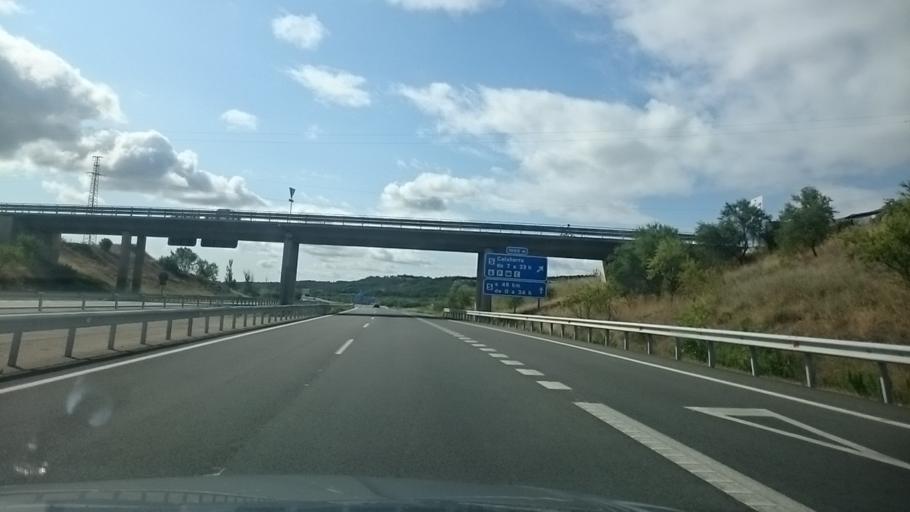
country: ES
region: La Rioja
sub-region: Provincia de La Rioja
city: Calahorra
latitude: 42.3033
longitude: -1.9810
